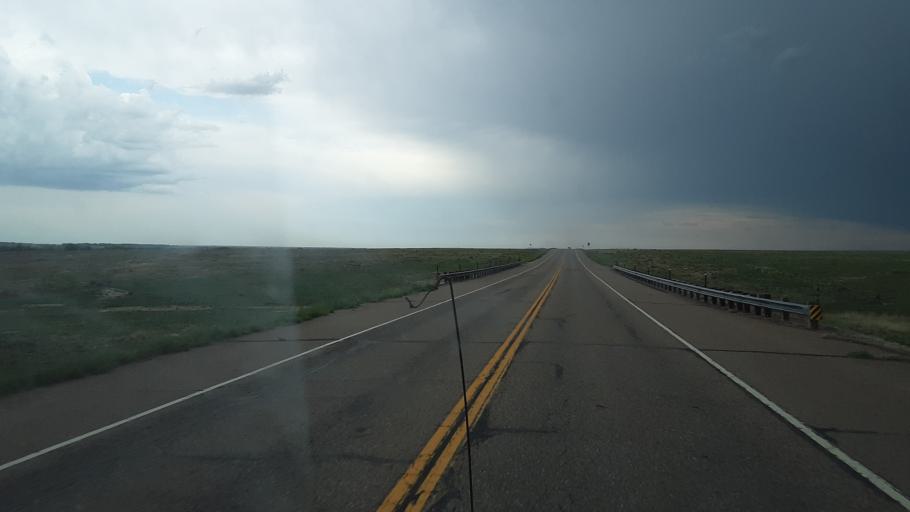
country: US
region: Colorado
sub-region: Bent County
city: Las Animas
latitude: 38.0436
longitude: -103.3811
